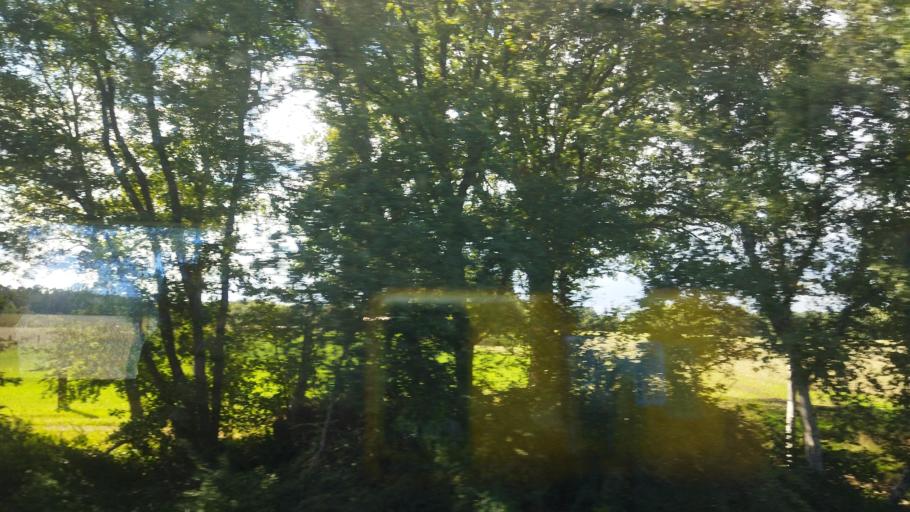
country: DE
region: Lower Saxony
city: Salzbergen
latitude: 52.3622
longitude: 7.3259
